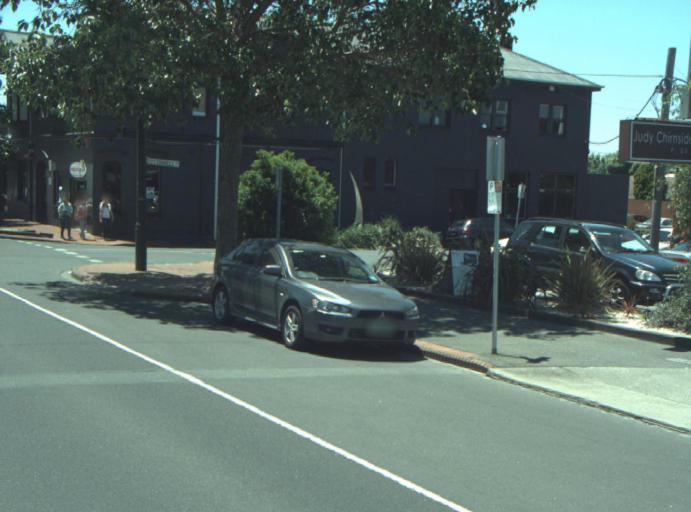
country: AU
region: Victoria
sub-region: Greater Geelong
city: Geelong West
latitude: -38.1393
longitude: 144.3486
